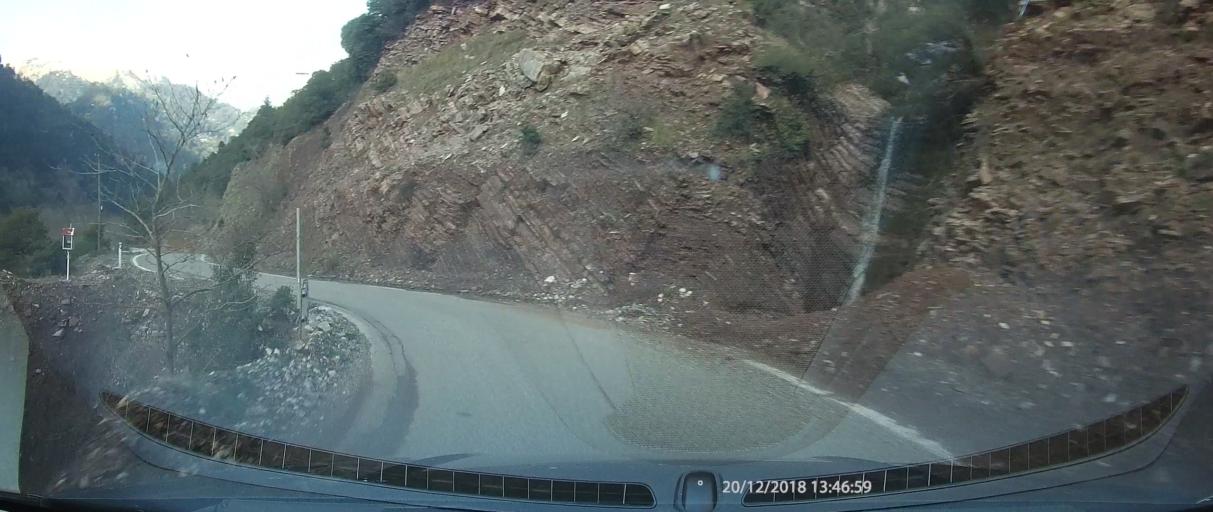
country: GR
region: West Greece
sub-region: Nomos Aitolias kai Akarnanias
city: Thermo
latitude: 38.6781
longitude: 21.6168
